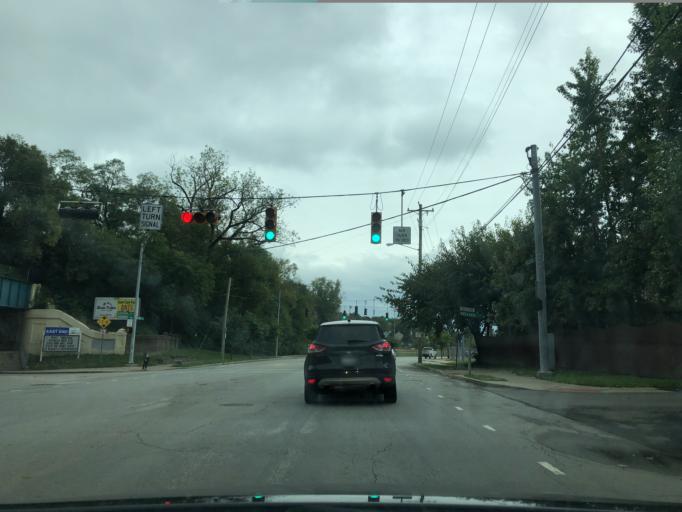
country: US
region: Kentucky
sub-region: Campbell County
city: Dayton
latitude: 39.1169
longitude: -84.4410
